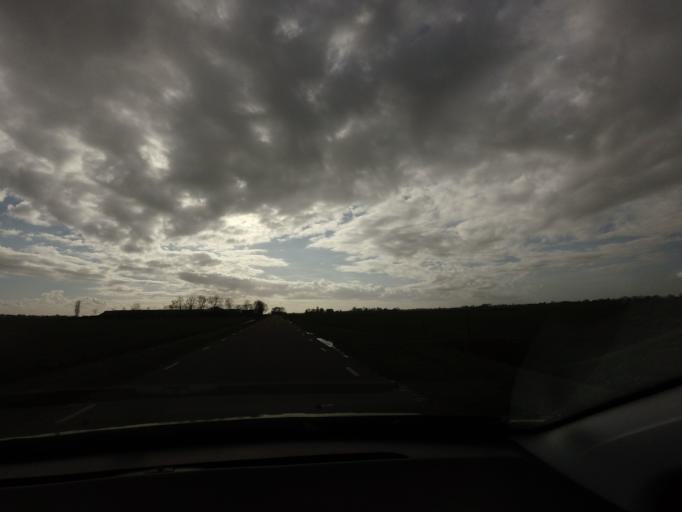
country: NL
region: Friesland
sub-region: Gemeente Boarnsterhim
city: Jirnsum
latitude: 53.0717
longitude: 5.7683
